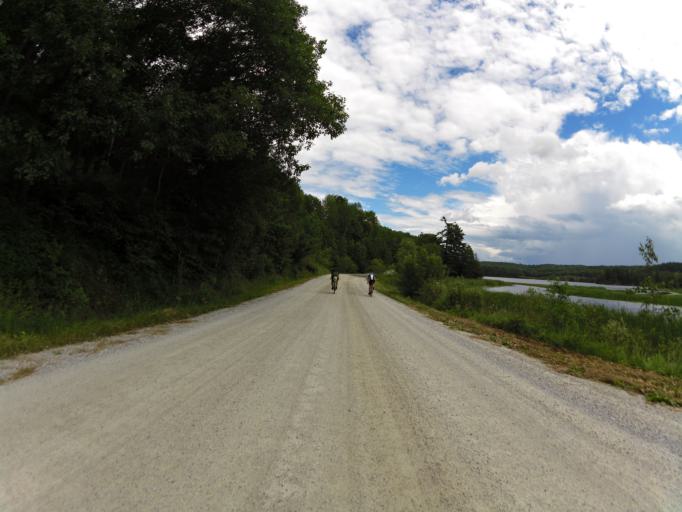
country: CA
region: Ontario
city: Renfrew
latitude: 45.1359
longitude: -76.6480
